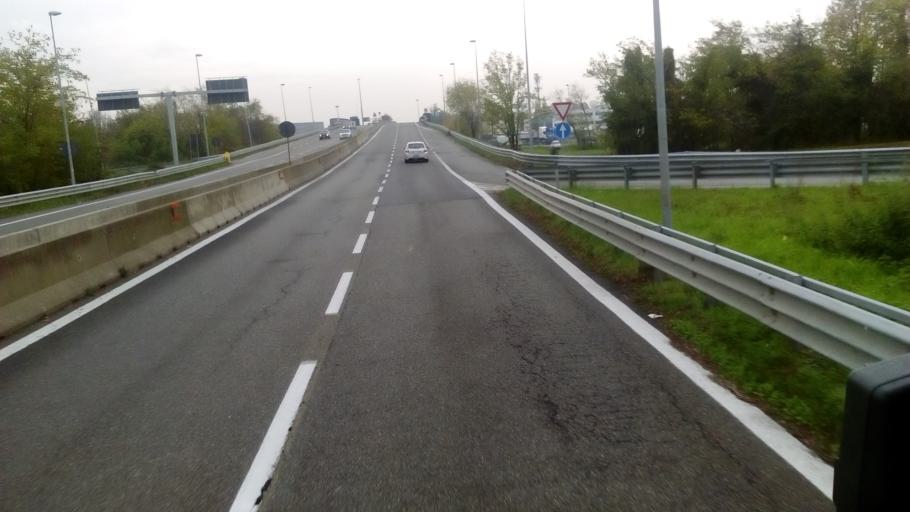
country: IT
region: Lombardy
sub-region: Provincia di Bergamo
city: Orio al Serio
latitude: 45.6685
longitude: 9.6874
